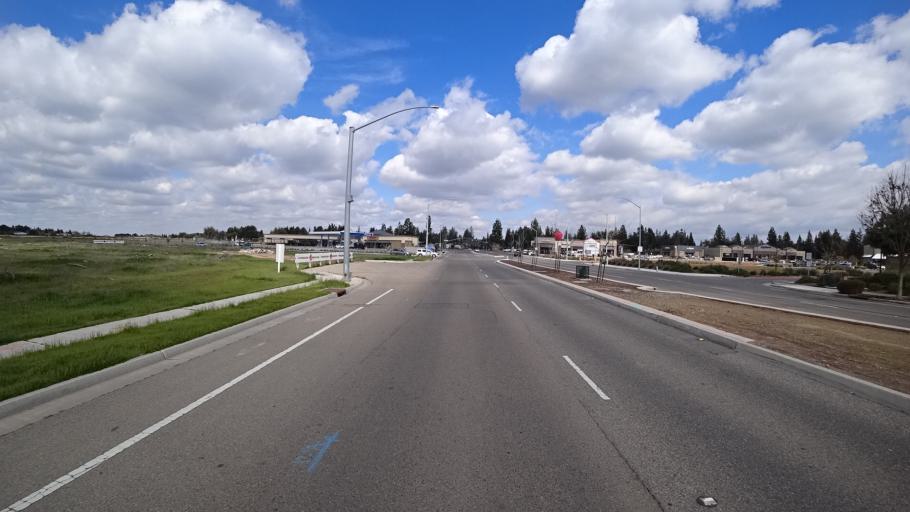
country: US
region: California
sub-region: Fresno County
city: West Park
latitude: 36.8352
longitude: -119.8626
